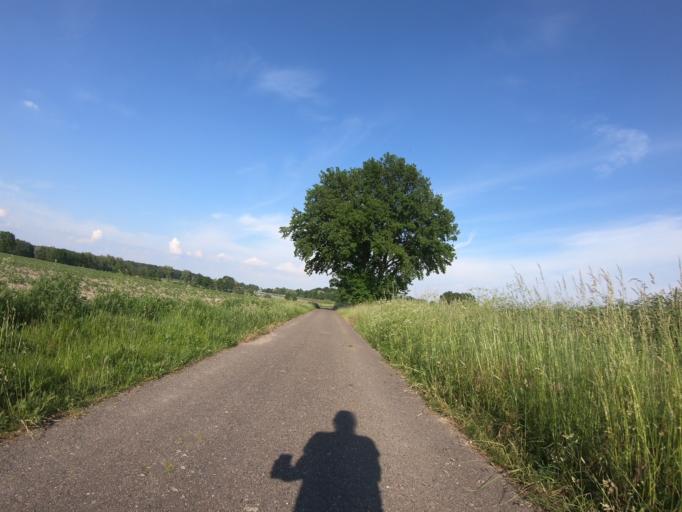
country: DE
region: Lower Saxony
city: Calberlah
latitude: 52.4075
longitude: 10.6130
